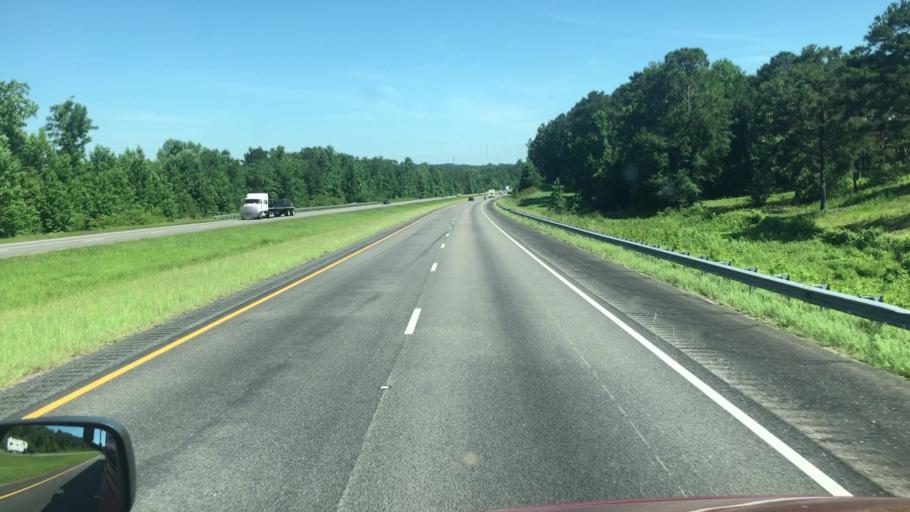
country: US
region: Alabama
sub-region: Autauga County
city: Pine Level
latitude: 32.5899
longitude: -86.4749
